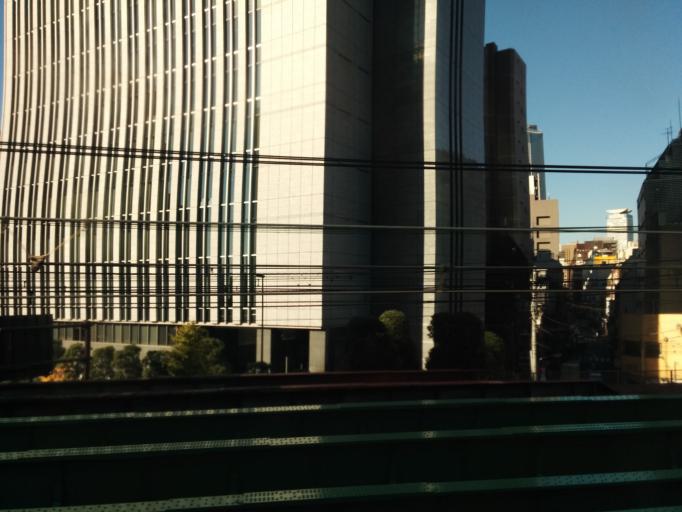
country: JP
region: Tokyo
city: Tokyo
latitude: 35.6641
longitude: 139.7586
